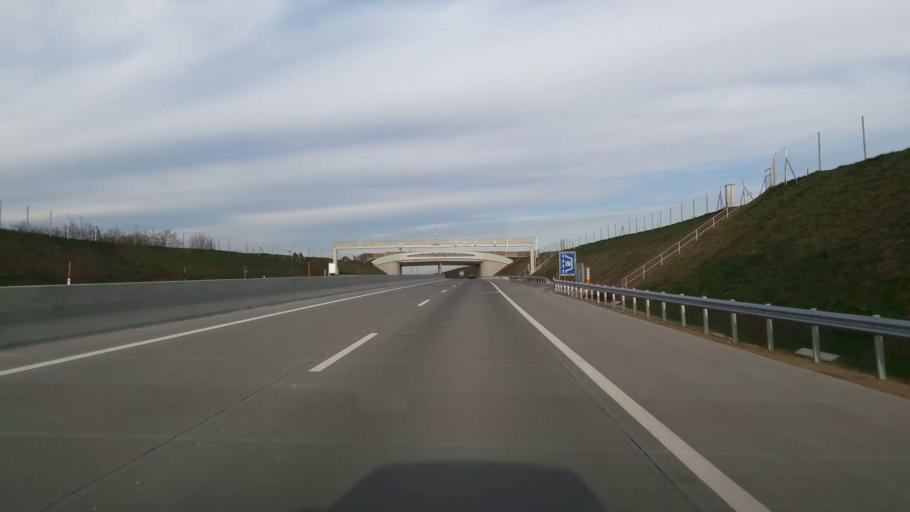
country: AT
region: Lower Austria
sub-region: Politischer Bezirk Mistelbach
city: Wilfersdorf
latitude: 48.5837
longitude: 16.6256
